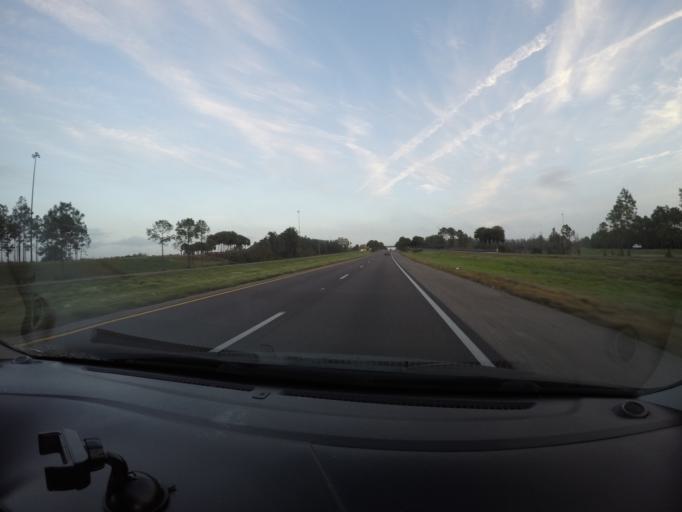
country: US
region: Florida
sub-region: Orange County
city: Conway
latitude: 28.4459
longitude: -81.2302
